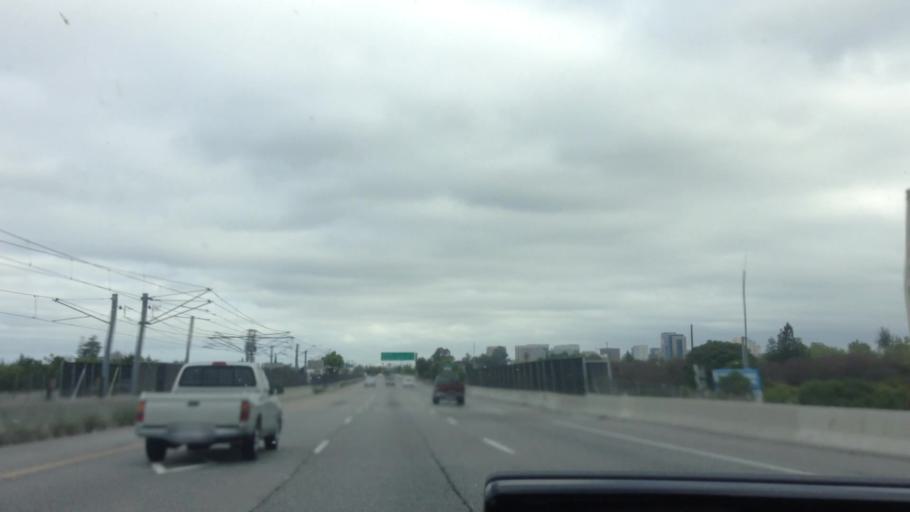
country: US
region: California
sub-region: Santa Clara County
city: San Jose
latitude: 37.3095
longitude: -121.8827
